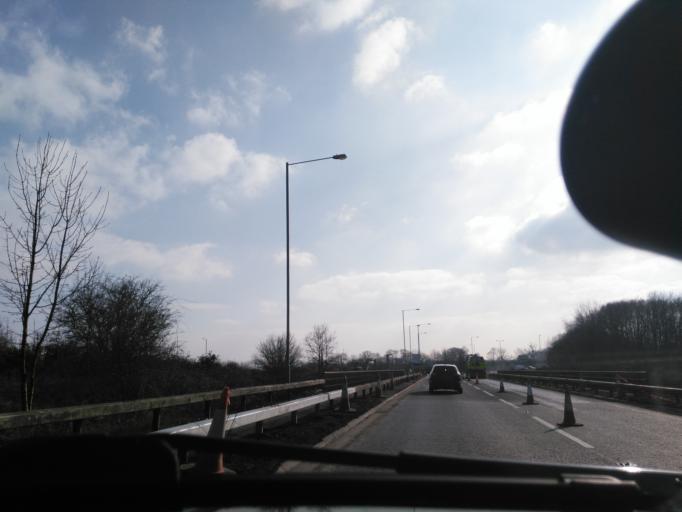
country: GB
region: England
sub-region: Wiltshire
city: Chippenham
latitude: 51.5156
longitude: -2.1207
